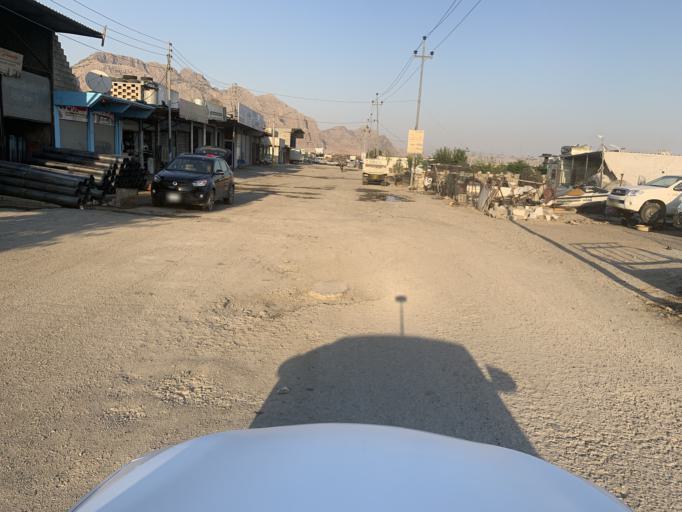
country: IQ
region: As Sulaymaniyah
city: Raniye
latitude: 36.2447
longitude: 44.8871
